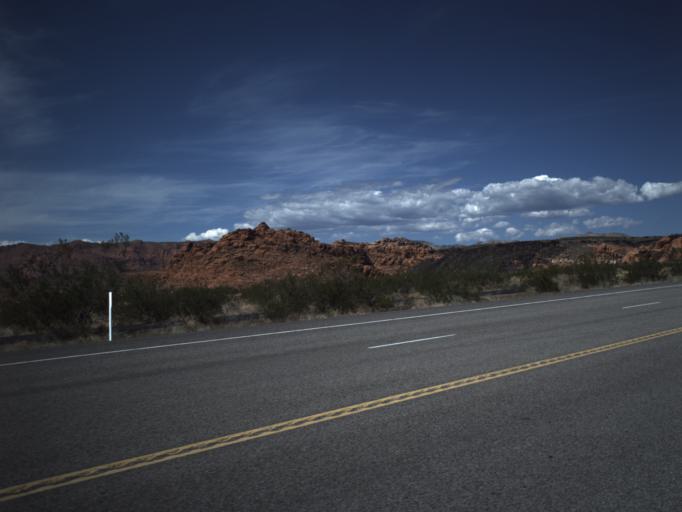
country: US
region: Utah
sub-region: Washington County
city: Santa Clara
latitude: 37.1497
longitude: -113.6076
